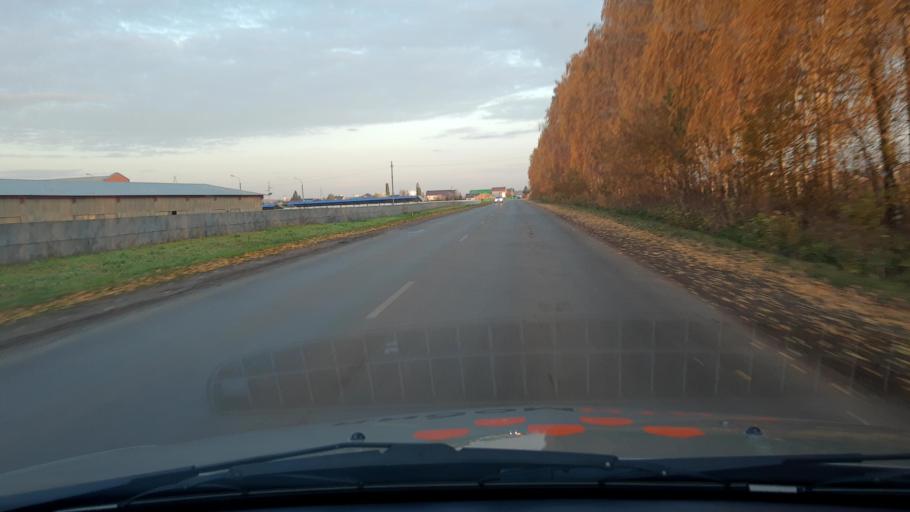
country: RU
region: Bashkortostan
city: Ufa
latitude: 54.8252
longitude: 55.9822
